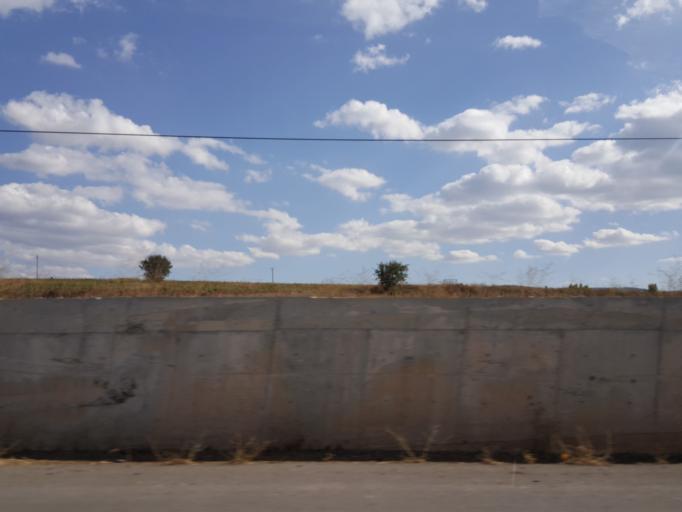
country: TR
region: Tokat
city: Sulusaray
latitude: 39.9802
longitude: 36.0620
